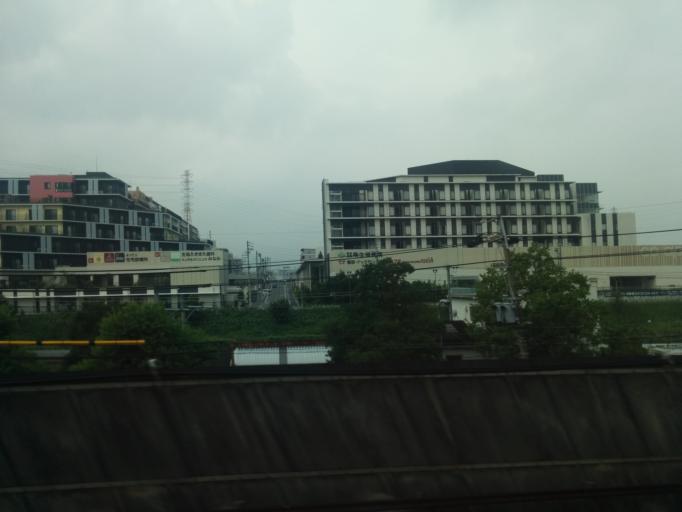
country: JP
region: Aichi
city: Obu
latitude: 35.0562
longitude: 136.9484
